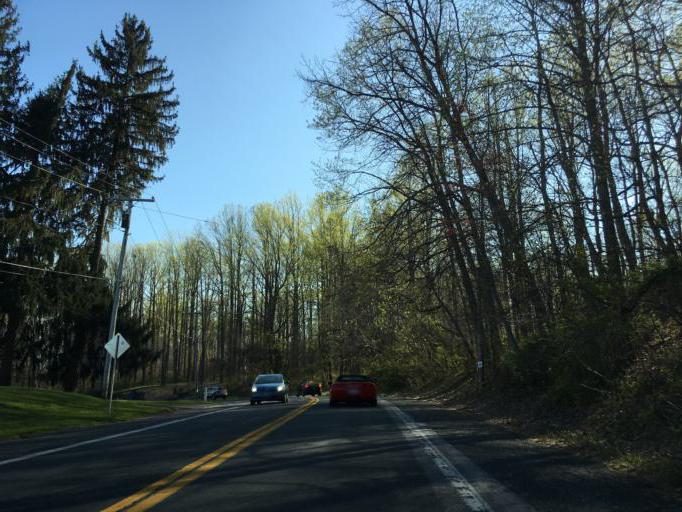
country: US
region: Maryland
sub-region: Baltimore County
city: Perry Hall
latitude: 39.4638
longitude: -76.4902
